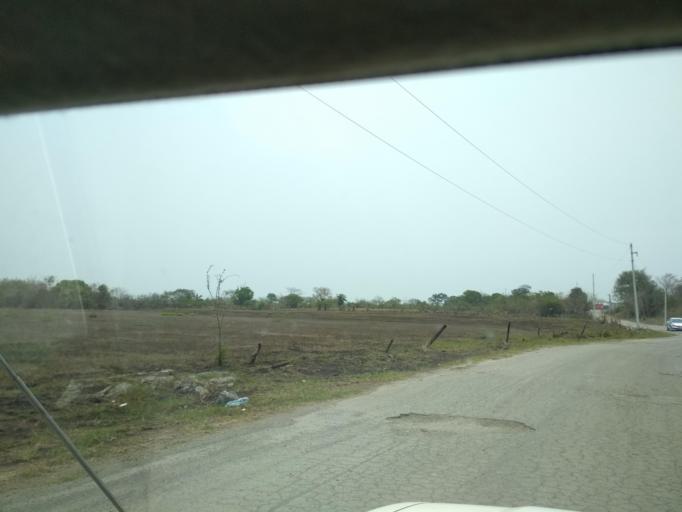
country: MX
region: Veracruz
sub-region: Veracruz
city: Delfino Victoria (Santa Fe)
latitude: 19.2012
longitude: -96.2584
